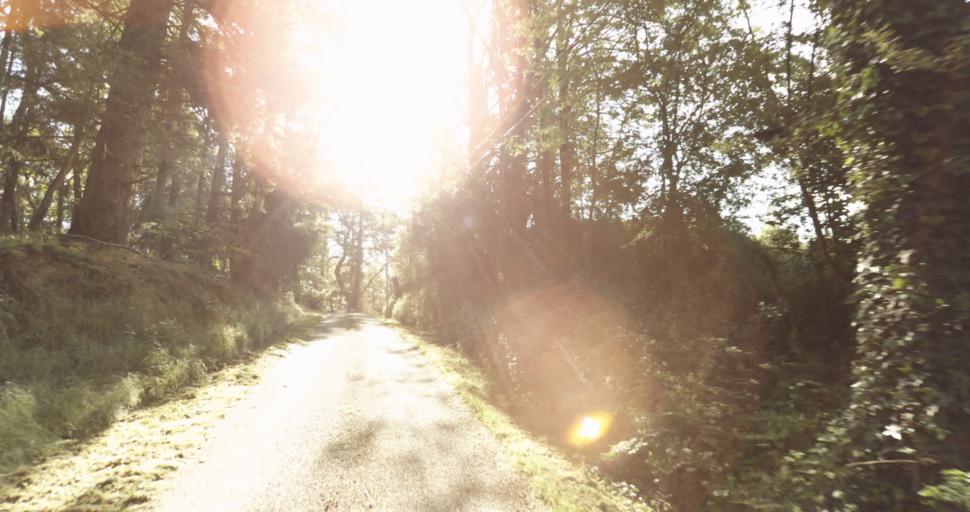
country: FR
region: Limousin
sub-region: Departement de la Haute-Vienne
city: Le Vigen
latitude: 45.7470
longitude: 1.2960
